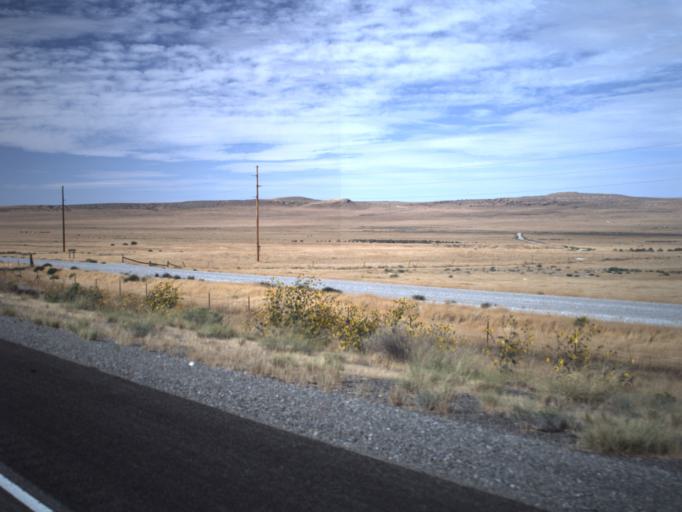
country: US
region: Utah
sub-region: Tooele County
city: Grantsville
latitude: 40.7956
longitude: -112.9492
